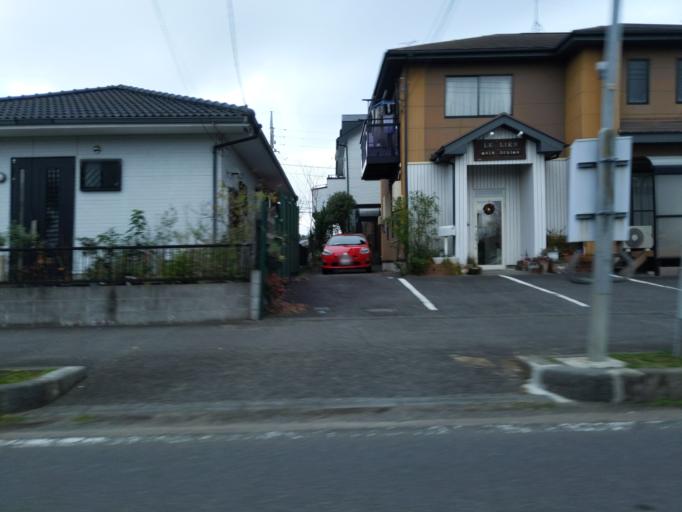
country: JP
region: Ibaraki
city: Ryugasaki
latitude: 35.9289
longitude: 140.2015
